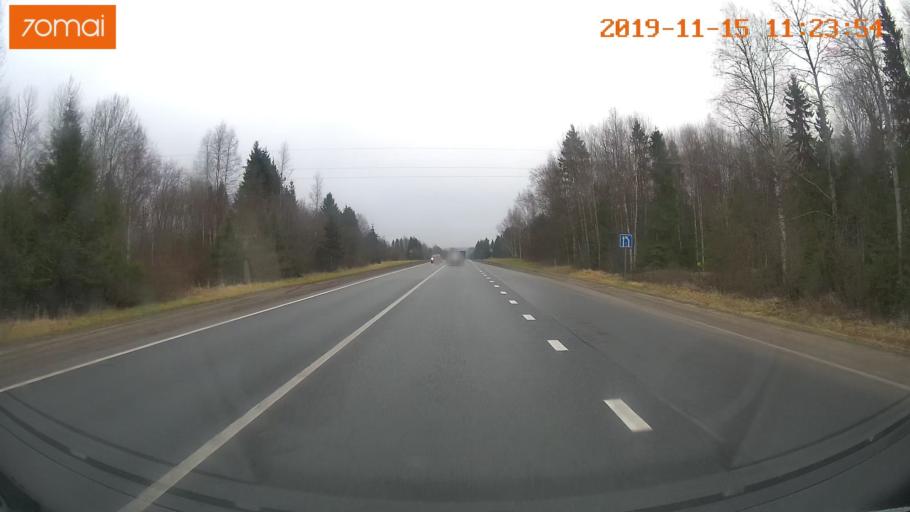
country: RU
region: Vologda
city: Molochnoye
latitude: 59.1543
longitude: 39.3934
